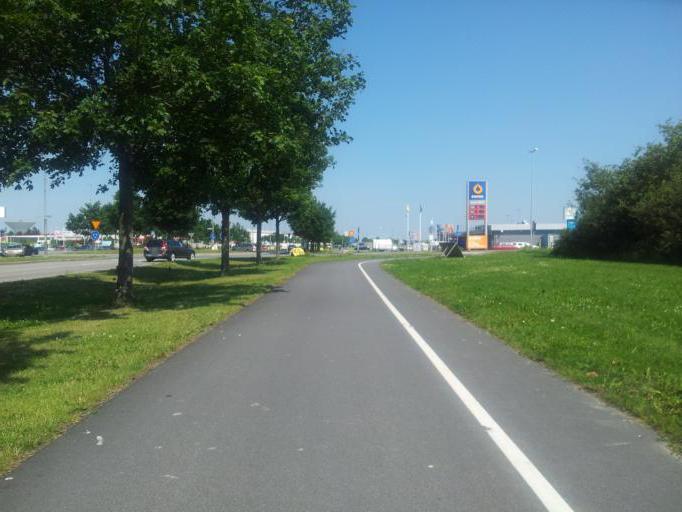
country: SE
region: Uppsala
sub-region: Uppsala Kommun
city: Saevja
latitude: 59.8449
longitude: 17.6905
